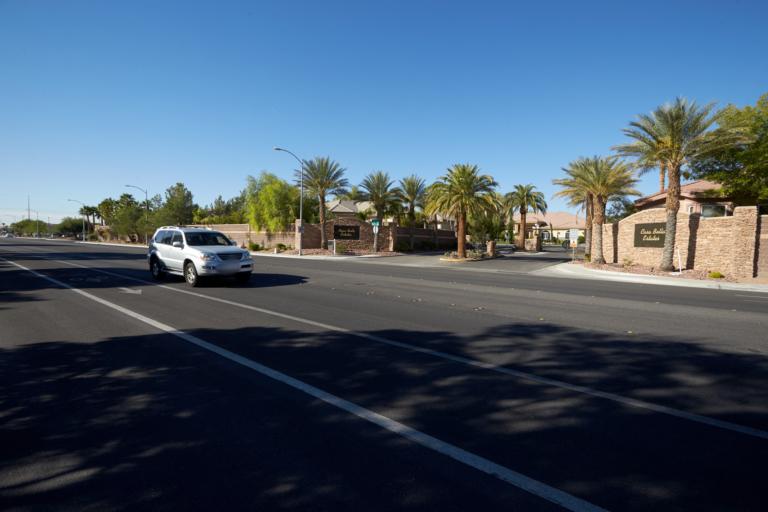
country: US
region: Nevada
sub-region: Clark County
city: Spring Valley
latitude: 36.1469
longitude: -115.2701
